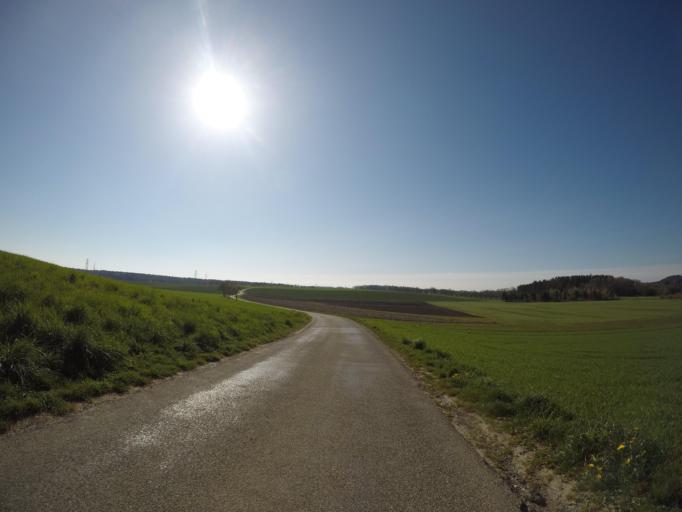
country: DE
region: Baden-Wuerttemberg
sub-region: Tuebingen Region
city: Ebenweiler
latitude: 47.8970
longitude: 9.5171
